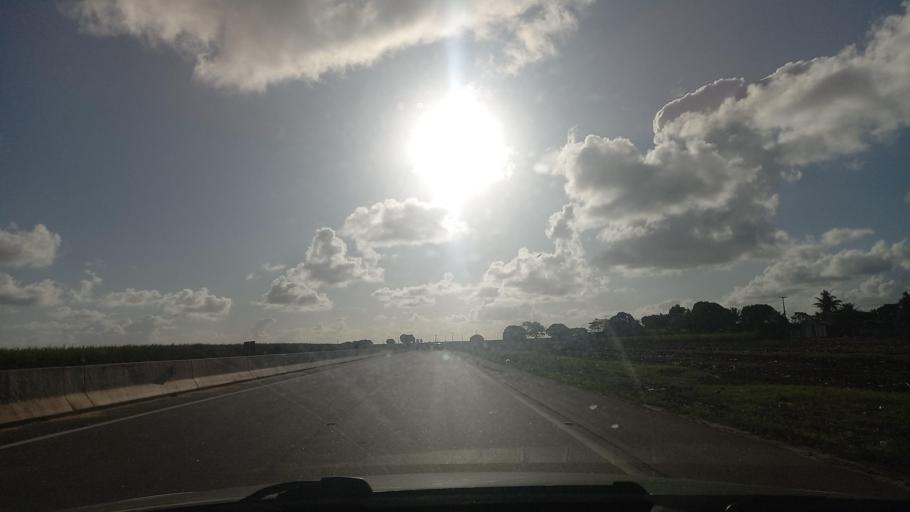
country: BR
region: Alagoas
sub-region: Sao Miguel Dos Campos
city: Sao Miguel dos Campos
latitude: -9.8076
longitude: -36.1177
